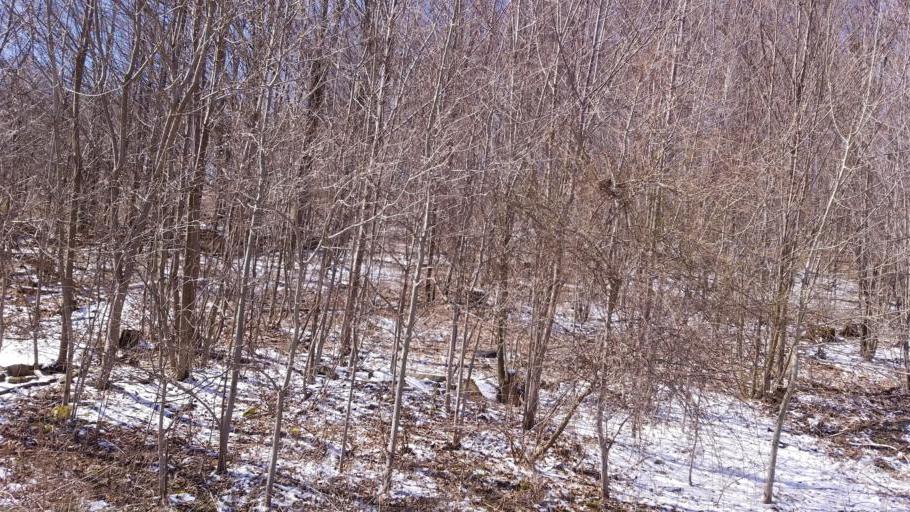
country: US
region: Pennsylvania
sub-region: Tioga County
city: Westfield
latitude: 41.9527
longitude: -77.7251
